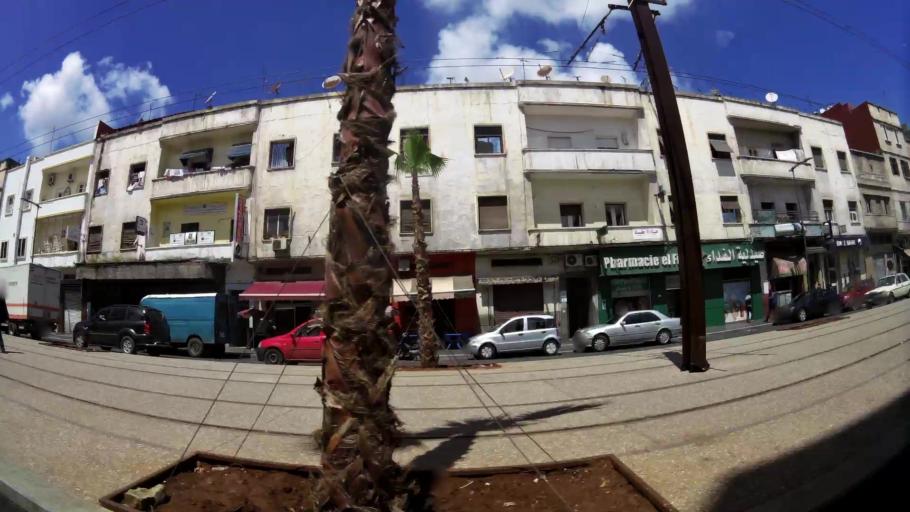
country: MA
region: Grand Casablanca
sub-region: Casablanca
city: Casablanca
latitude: 33.5673
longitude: -7.6059
